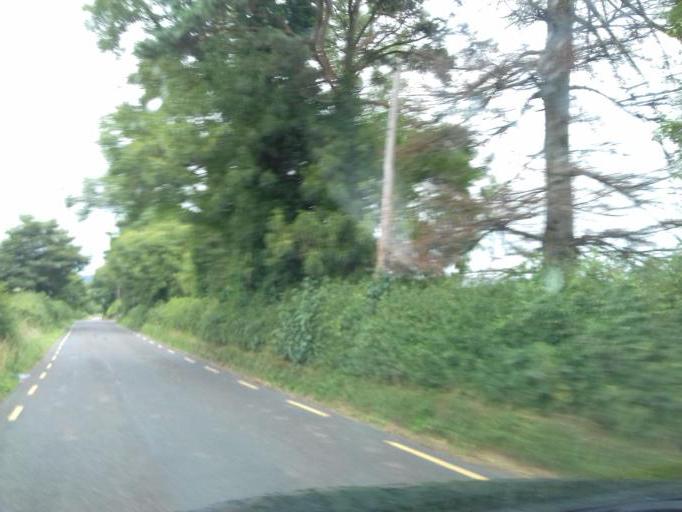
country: IE
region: Leinster
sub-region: County Carlow
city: Bagenalstown
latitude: 52.6231
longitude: -7.0402
